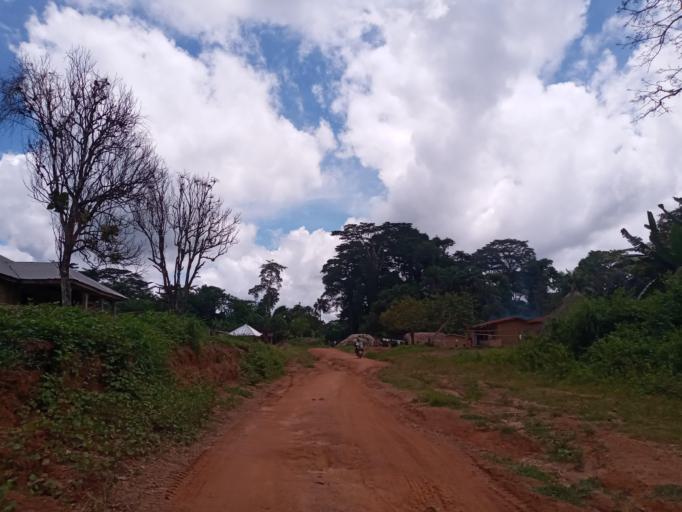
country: SL
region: Eastern Province
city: Tombu
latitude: 8.6288
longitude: -10.8345
